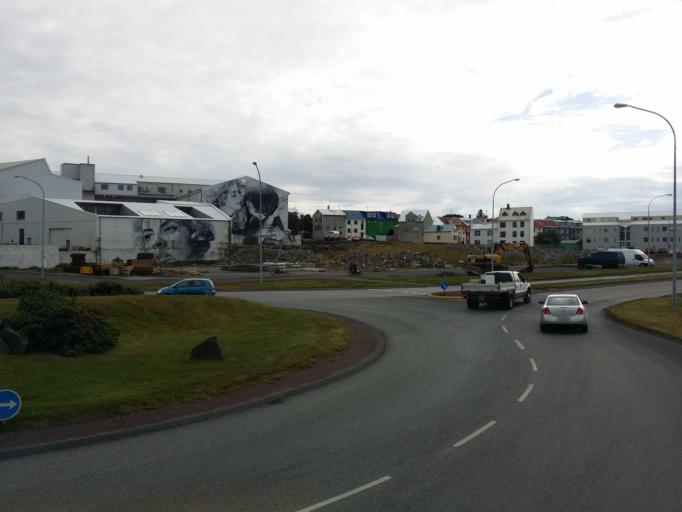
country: IS
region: Capital Region
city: Seltjarnarnes
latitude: 64.1530
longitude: -21.9531
